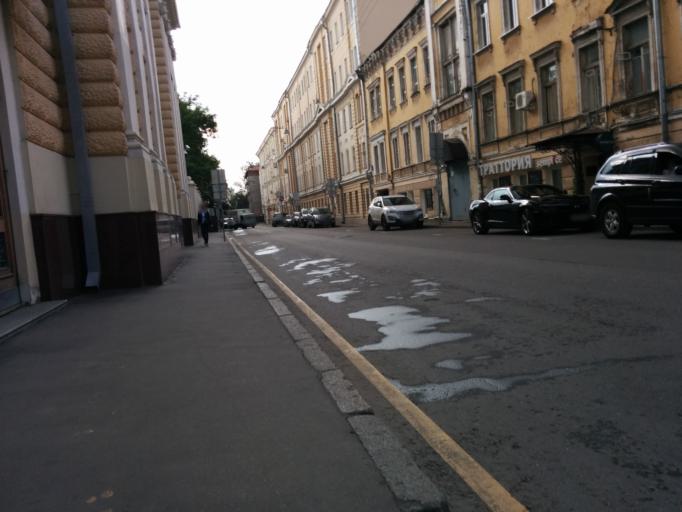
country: RU
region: Moscow
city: Moscow
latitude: 55.7641
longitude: 37.6461
